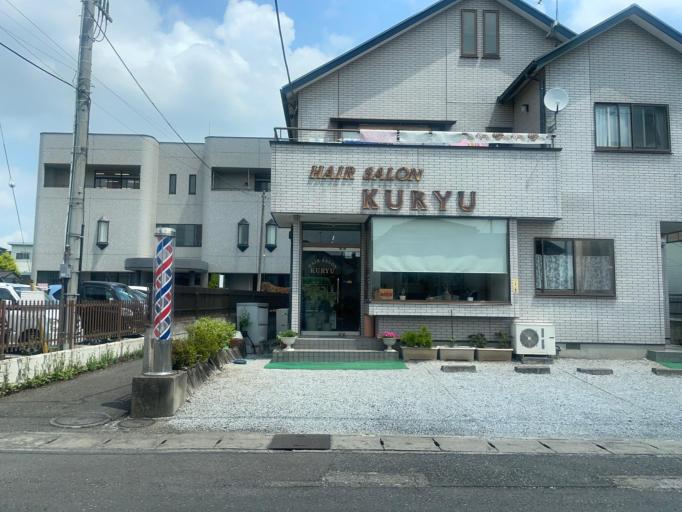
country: JP
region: Tochigi
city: Tochigi
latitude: 36.3857
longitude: 139.7292
